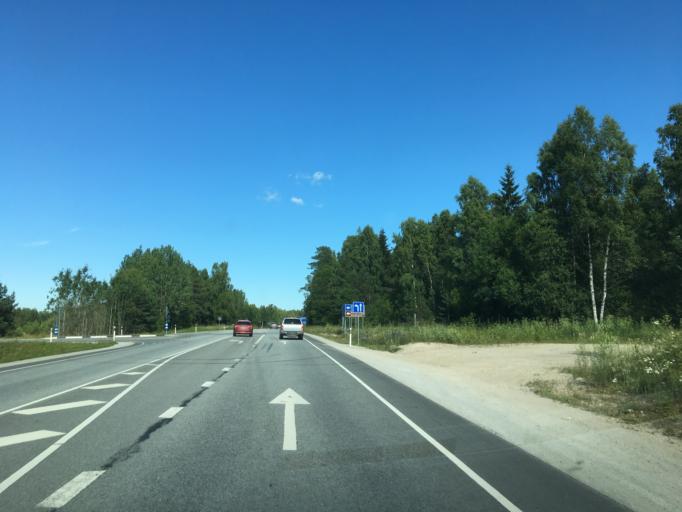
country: EE
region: Harju
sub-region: Keila linn
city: Keila
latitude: 59.2370
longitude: 24.4744
